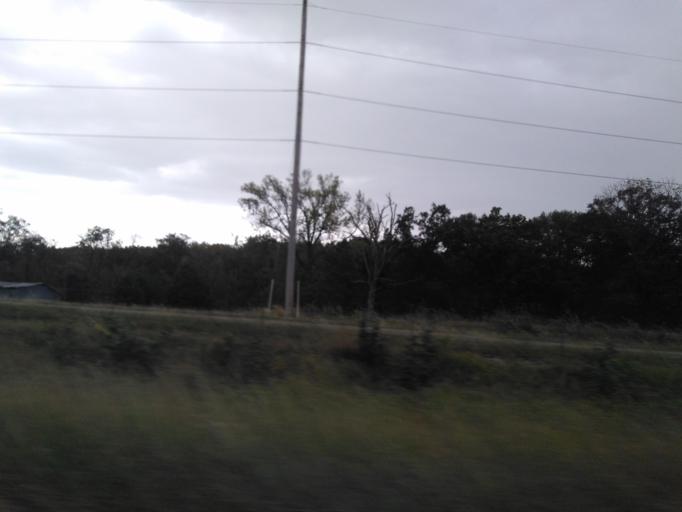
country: US
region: Illinois
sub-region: Bond County
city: Greenville
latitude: 38.8455
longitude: -89.4836
